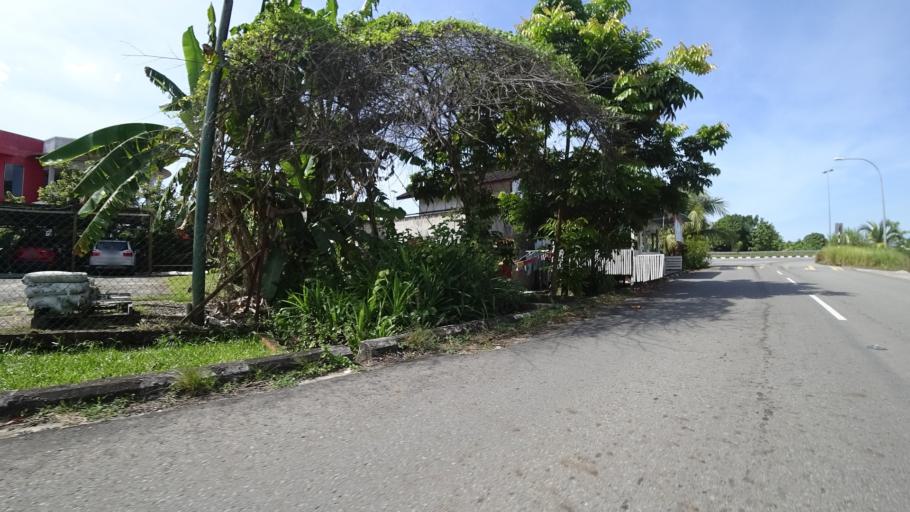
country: BN
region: Brunei and Muara
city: Bandar Seri Begawan
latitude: 4.8939
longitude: 114.8491
